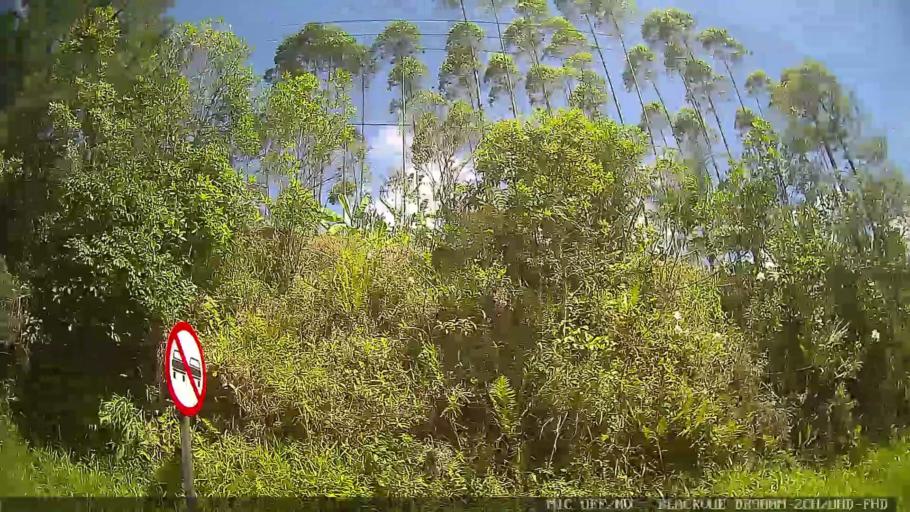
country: BR
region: Sao Paulo
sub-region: Mogi das Cruzes
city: Mogi das Cruzes
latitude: -23.6748
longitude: -46.1944
